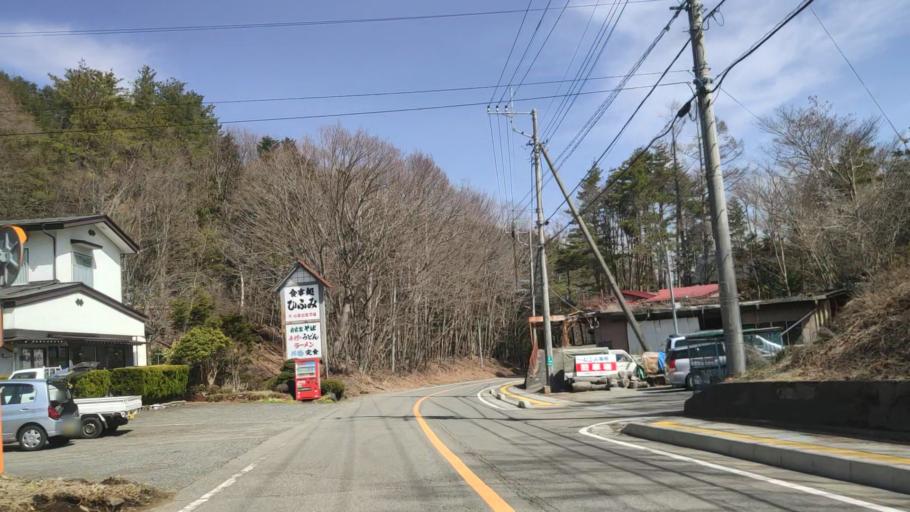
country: JP
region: Yamanashi
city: Fujikawaguchiko
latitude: 35.4924
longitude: 138.7284
